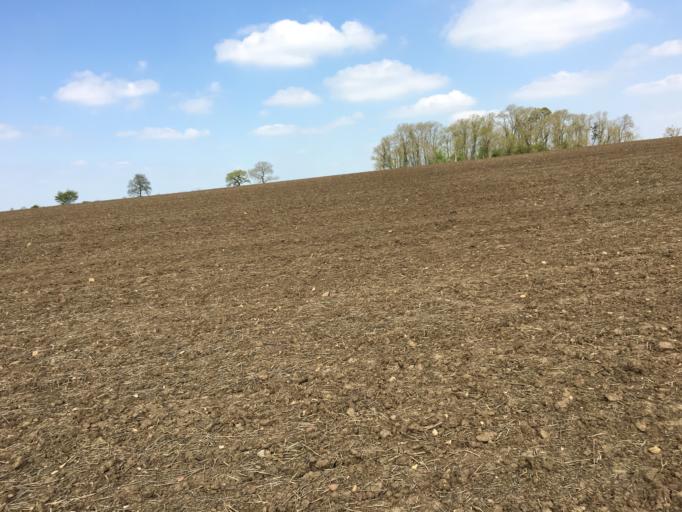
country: GB
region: England
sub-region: Leicestershire
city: Houghton on the Hill
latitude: 52.6075
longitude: -0.9948
